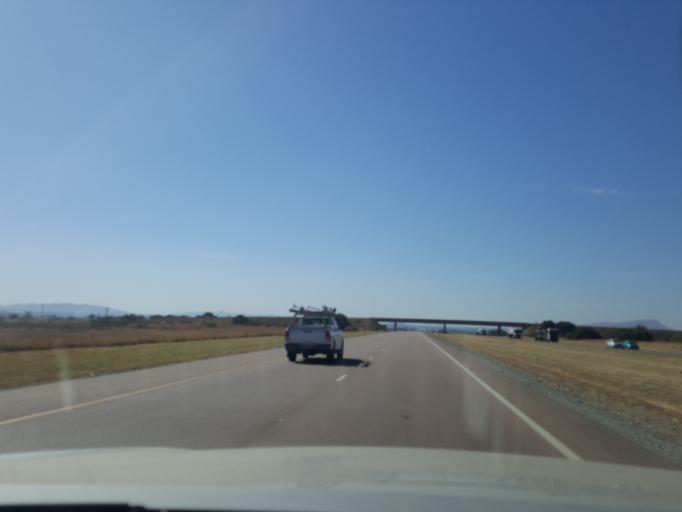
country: ZA
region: North-West
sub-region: Bojanala Platinum District Municipality
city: Brits
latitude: -25.6879
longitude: 27.7554
